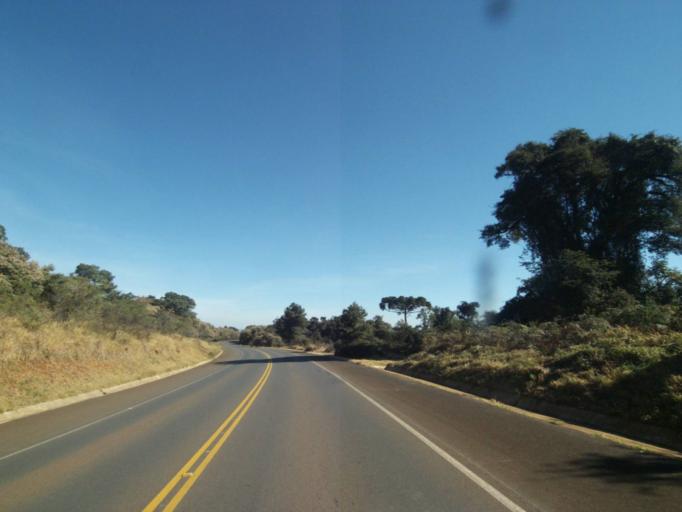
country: BR
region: Parana
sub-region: Tibagi
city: Tibagi
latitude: -24.4237
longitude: -50.3954
